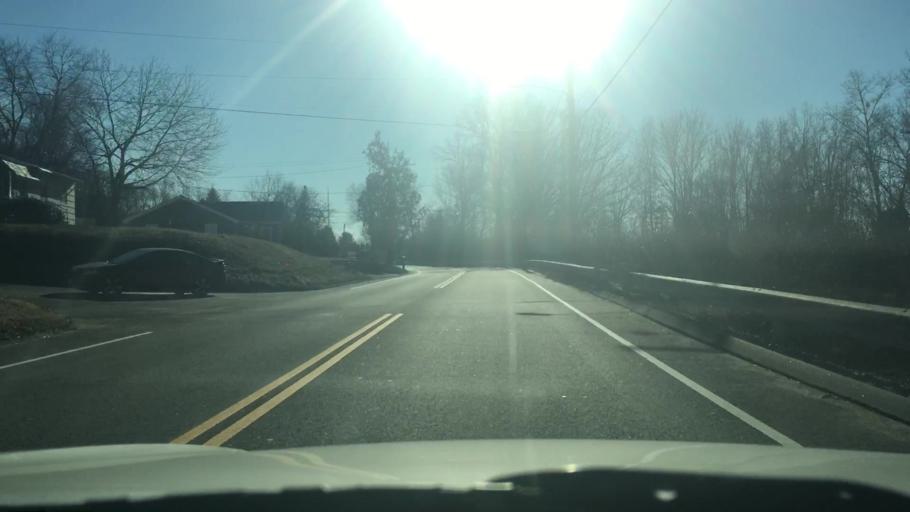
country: US
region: Massachusetts
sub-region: Hampden County
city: Ludlow
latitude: 42.1865
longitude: -72.5047
